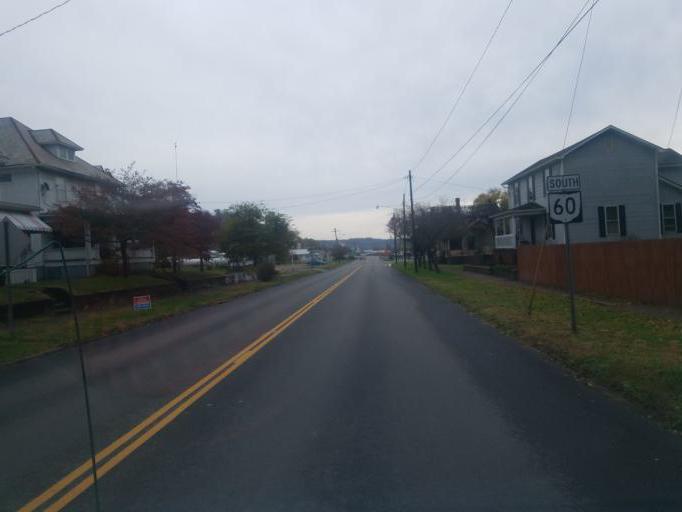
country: US
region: Ohio
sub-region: Washington County
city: Devola
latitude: 39.5279
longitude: -81.5059
